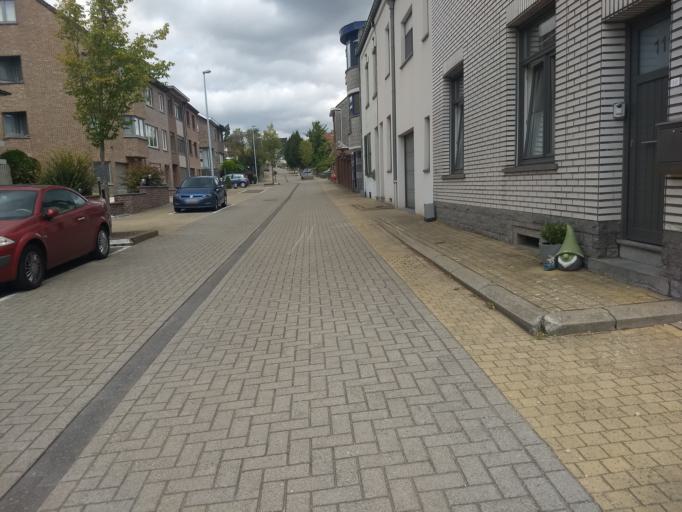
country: BE
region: Wallonia
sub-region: Province du Brabant Wallon
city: Tubize
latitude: 50.7170
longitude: 4.1956
